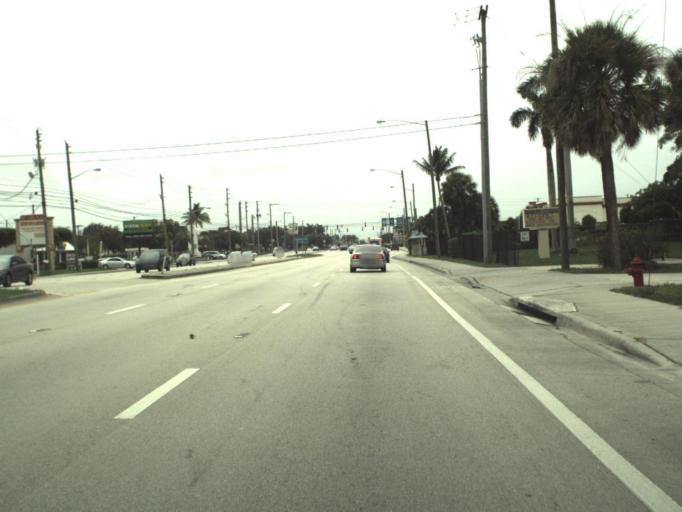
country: US
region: Florida
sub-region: Palm Beach County
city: Schall Circle
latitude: 26.7098
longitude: -80.1111
